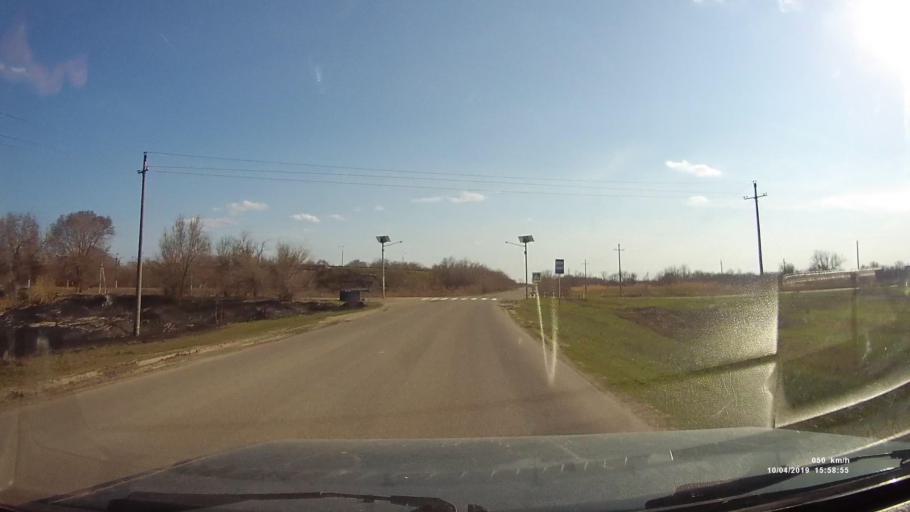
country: RU
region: Rostov
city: Masalovka
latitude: 48.3991
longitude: 40.2712
